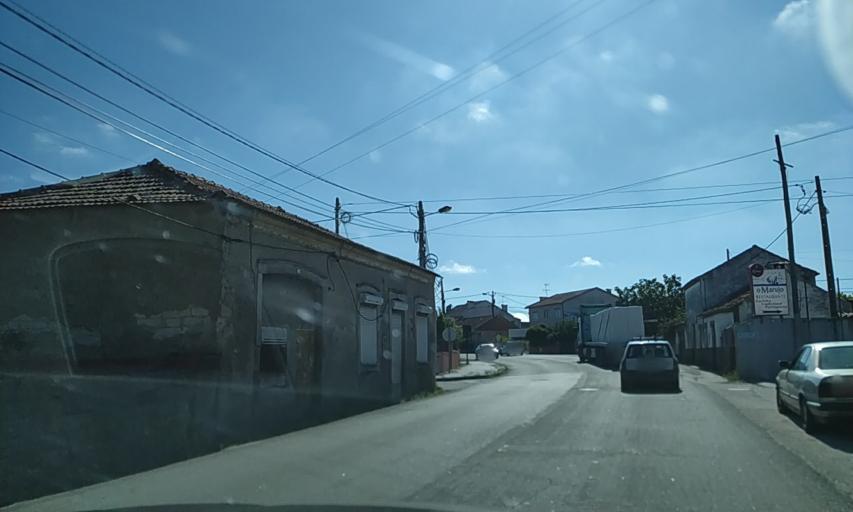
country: PT
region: Aveiro
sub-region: Aveiro
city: Eixo
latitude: 40.6788
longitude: -8.5968
